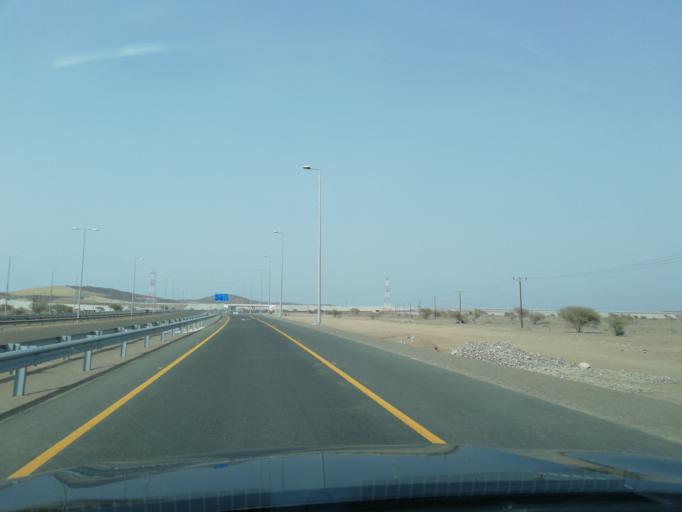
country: OM
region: Al Batinah
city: Al Liwa'
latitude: 24.3796
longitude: 56.5439
